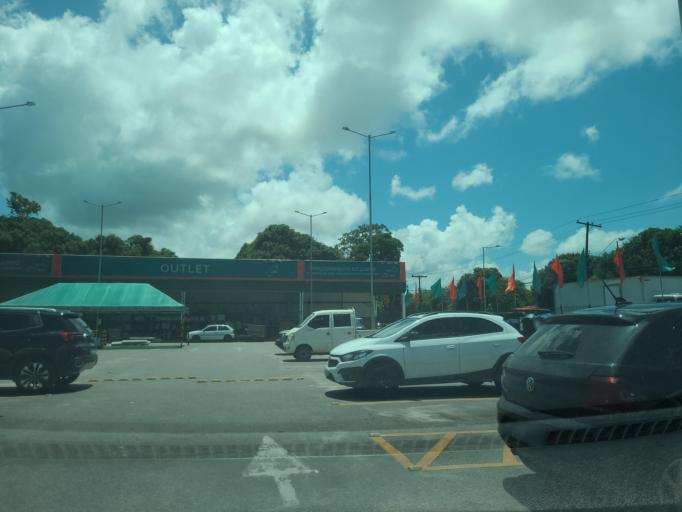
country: BR
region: Alagoas
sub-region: Satuba
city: Satuba
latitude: -9.5899
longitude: -35.7609
